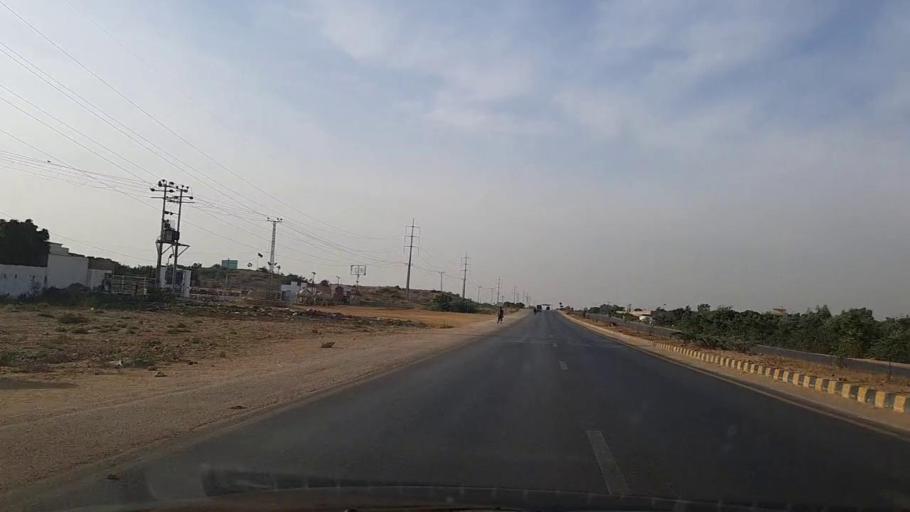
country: PK
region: Sindh
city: Gharo
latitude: 24.7591
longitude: 67.5595
